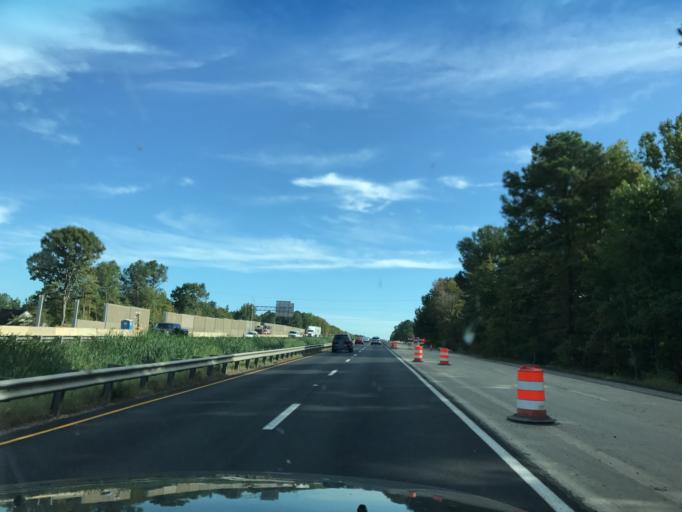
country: US
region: Virginia
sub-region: York County
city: Yorktown
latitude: 37.1646
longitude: -76.5452
